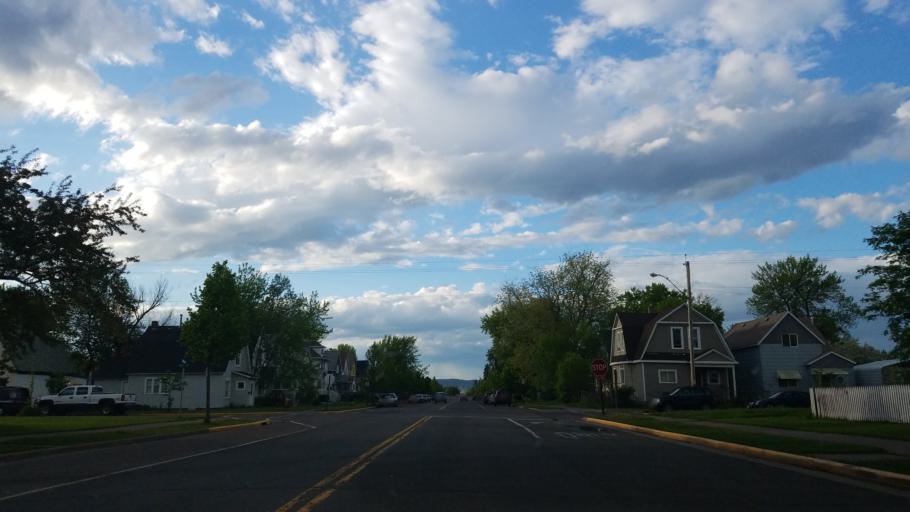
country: US
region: Wisconsin
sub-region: Douglas County
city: Superior
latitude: 46.7238
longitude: -92.0934
